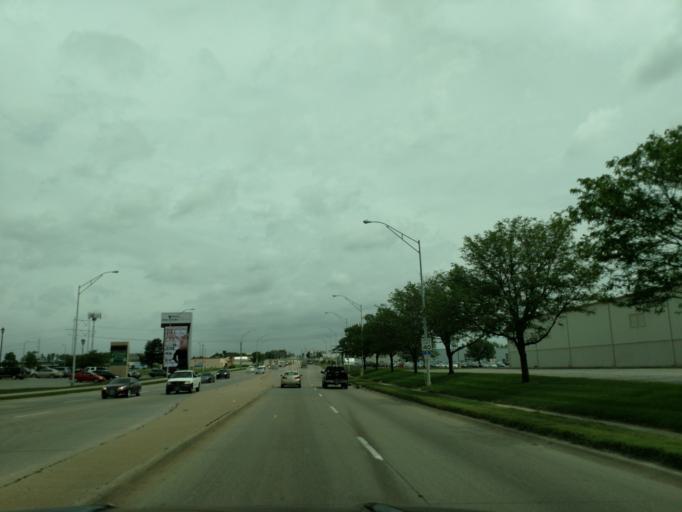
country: US
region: Nebraska
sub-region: Douglas County
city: Ralston
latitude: 41.2057
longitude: -96.0238
